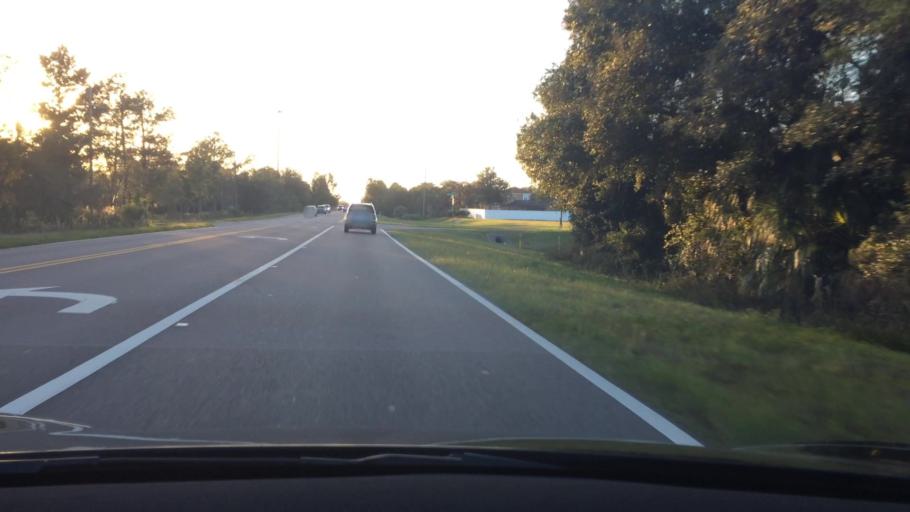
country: US
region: Florida
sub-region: Hillsborough County
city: Pebble Creek
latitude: 28.1713
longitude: -82.3852
